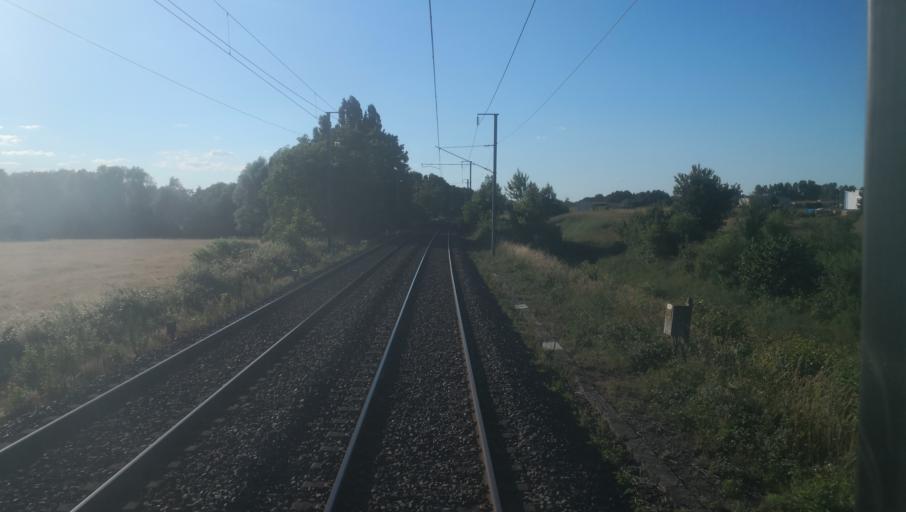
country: FR
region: Auvergne
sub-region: Departement de l'Allier
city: Avermes
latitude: 46.6064
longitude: 3.2959
